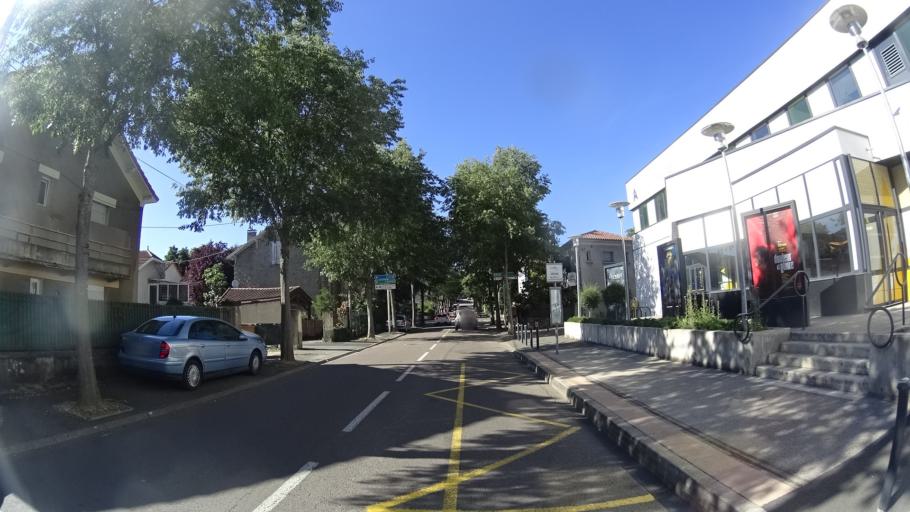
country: FR
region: Midi-Pyrenees
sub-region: Departement du Lot
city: Figeac
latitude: 44.6086
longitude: 2.0257
